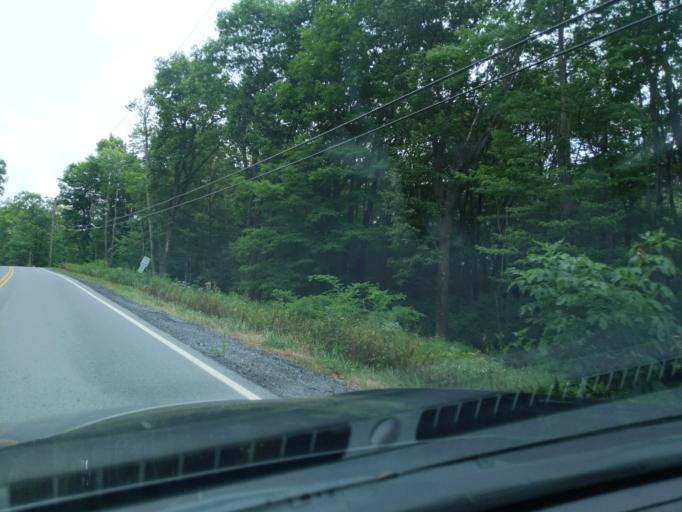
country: US
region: Pennsylvania
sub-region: Cambria County
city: Beaverdale
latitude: 40.2965
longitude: -78.5787
